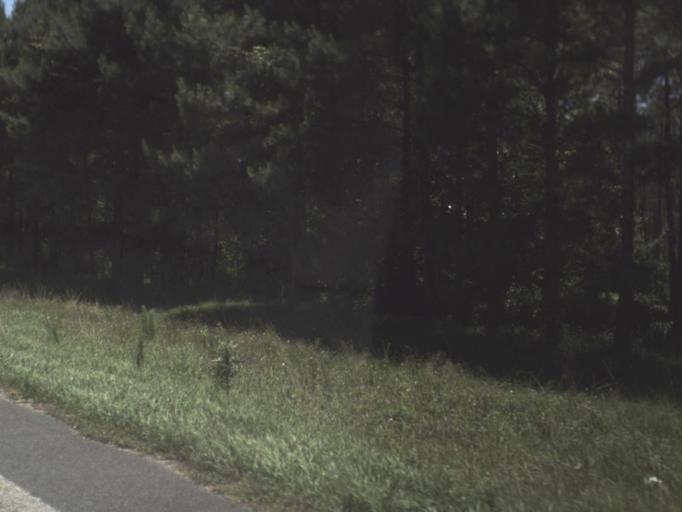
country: US
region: Florida
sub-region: Clay County
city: Bellair-Meadowbrook Terrace
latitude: 30.2307
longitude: -81.8439
